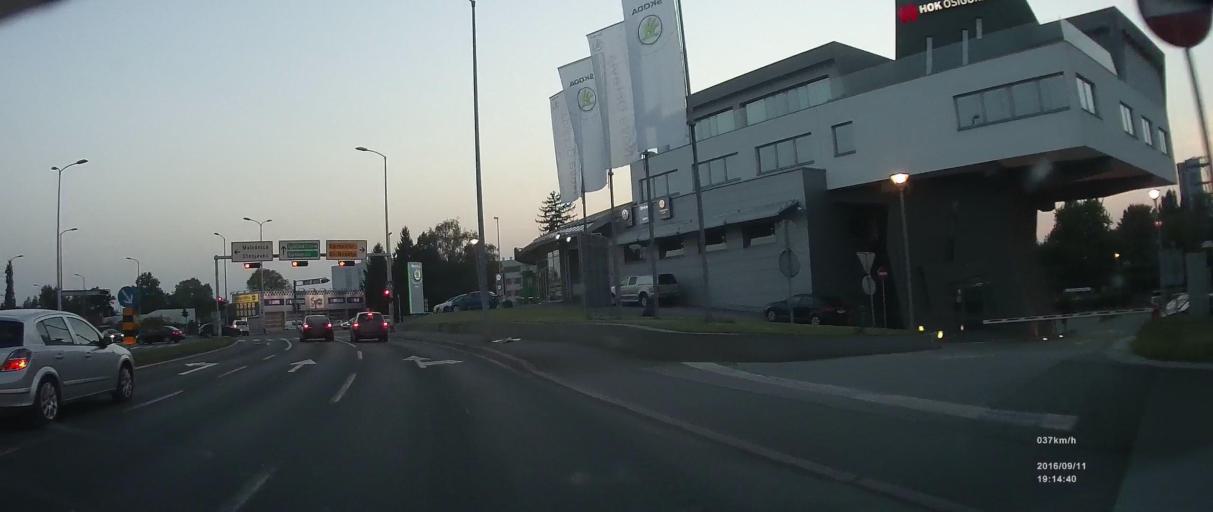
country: HR
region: Grad Zagreb
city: Stenjevec
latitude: 45.8130
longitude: 15.8614
